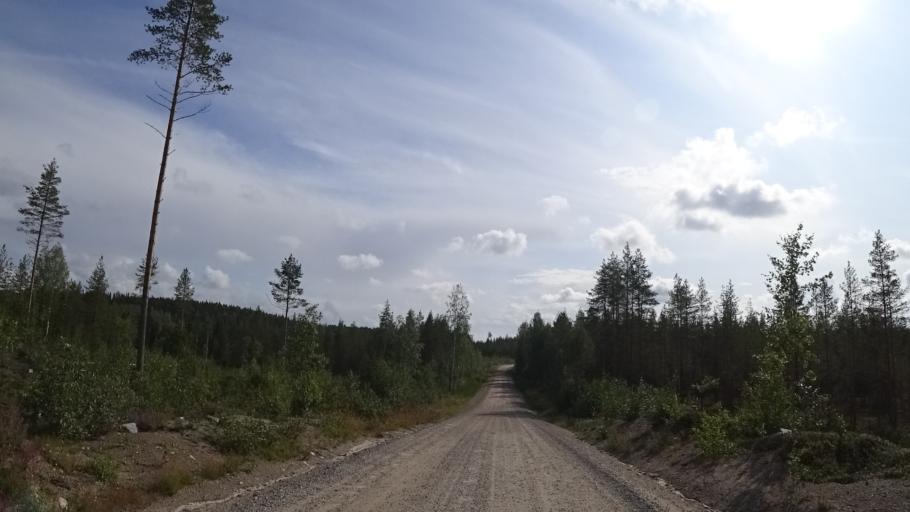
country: FI
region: North Karelia
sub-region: Pielisen Karjala
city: Lieksa
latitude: 63.5846
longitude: 30.1334
